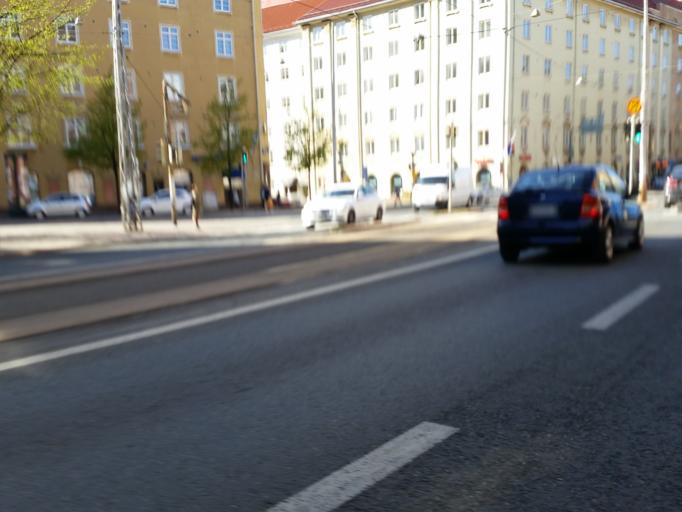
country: FI
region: Uusimaa
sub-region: Helsinki
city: Helsinki
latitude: 60.1749
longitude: 24.9220
